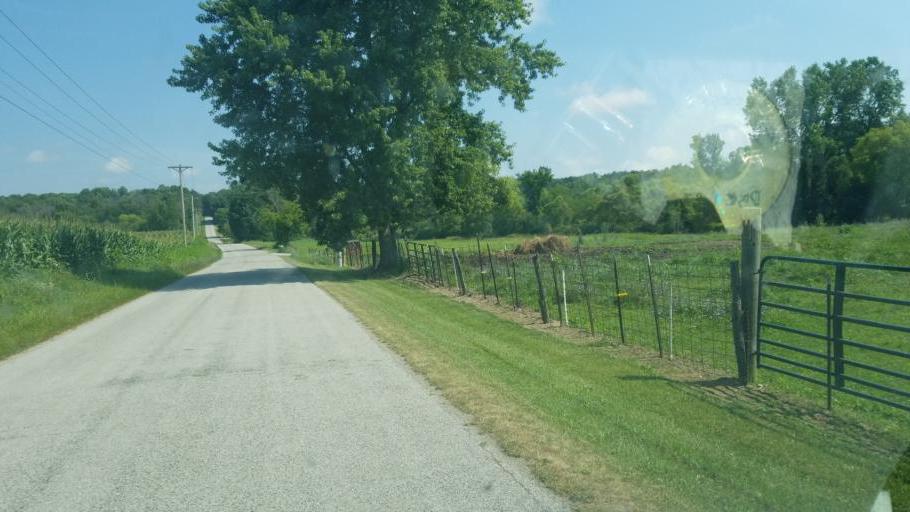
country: US
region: Ohio
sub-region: Knox County
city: Fredericktown
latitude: 40.4761
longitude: -82.6463
